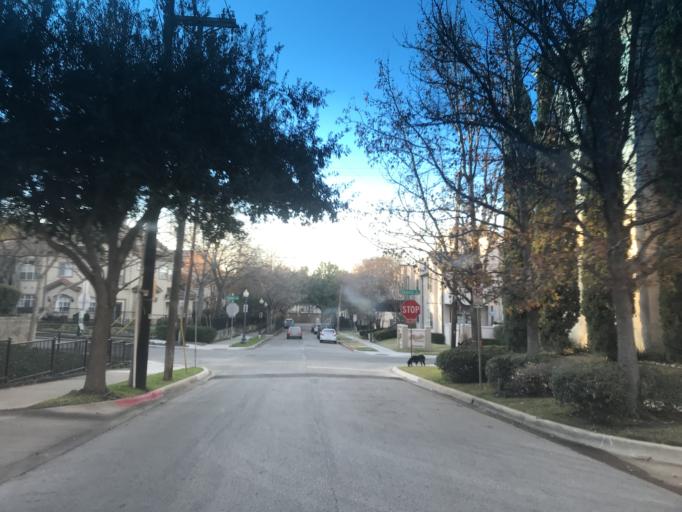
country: US
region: Texas
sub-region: Dallas County
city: Highland Park
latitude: 32.8110
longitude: -96.7965
